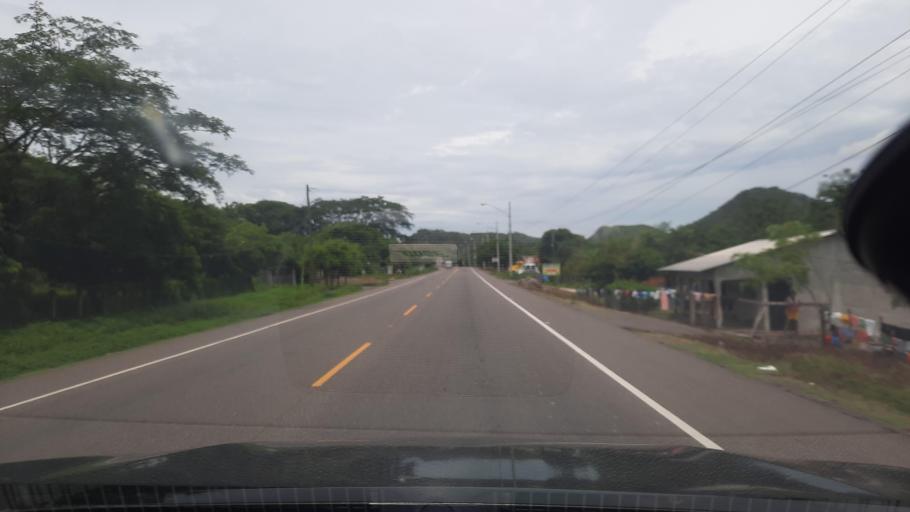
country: HN
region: Valle
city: Langue
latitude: 13.5840
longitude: -87.6897
